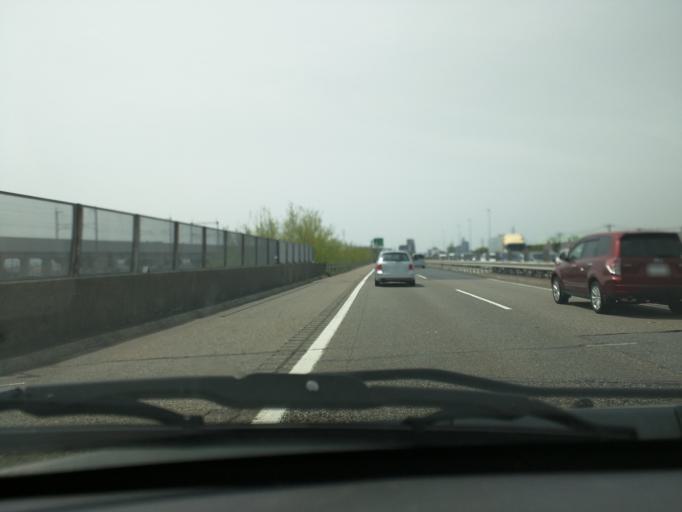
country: JP
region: Niigata
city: Tsubame
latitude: 37.6570
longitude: 138.9421
